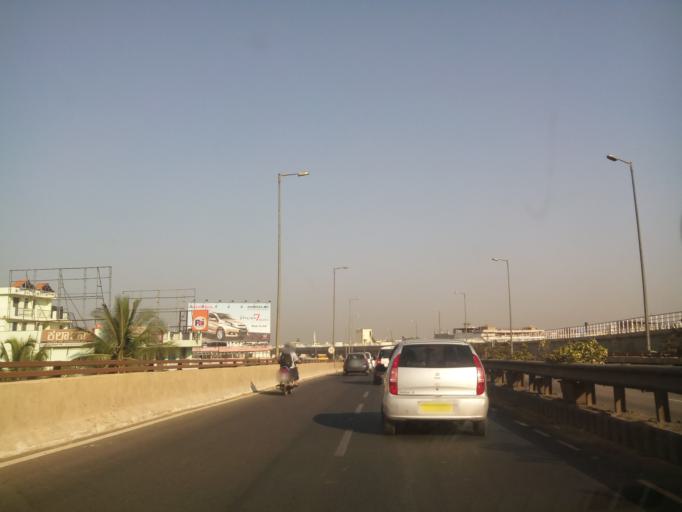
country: IN
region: Karnataka
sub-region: Bangalore Urban
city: Yelahanka
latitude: 13.0404
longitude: 77.5177
